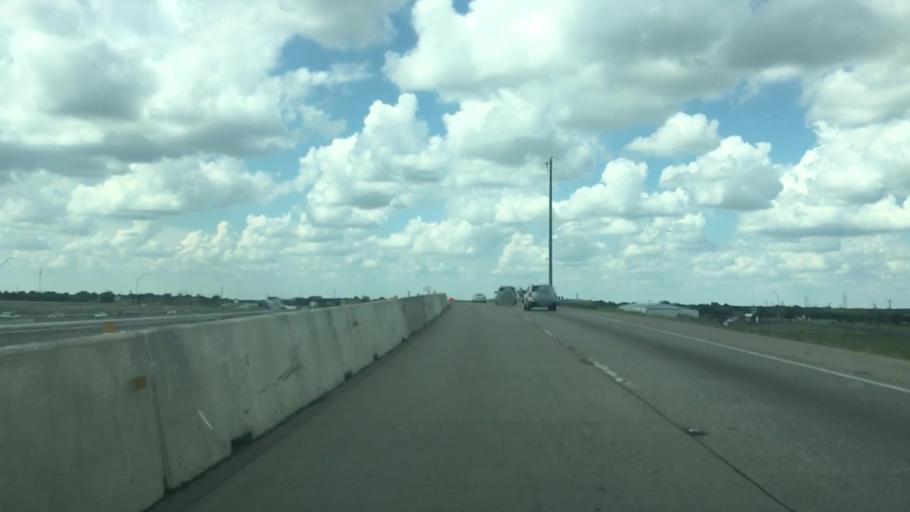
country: US
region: Texas
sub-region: Ellis County
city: Waxahachie
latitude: 32.3622
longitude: -96.8554
